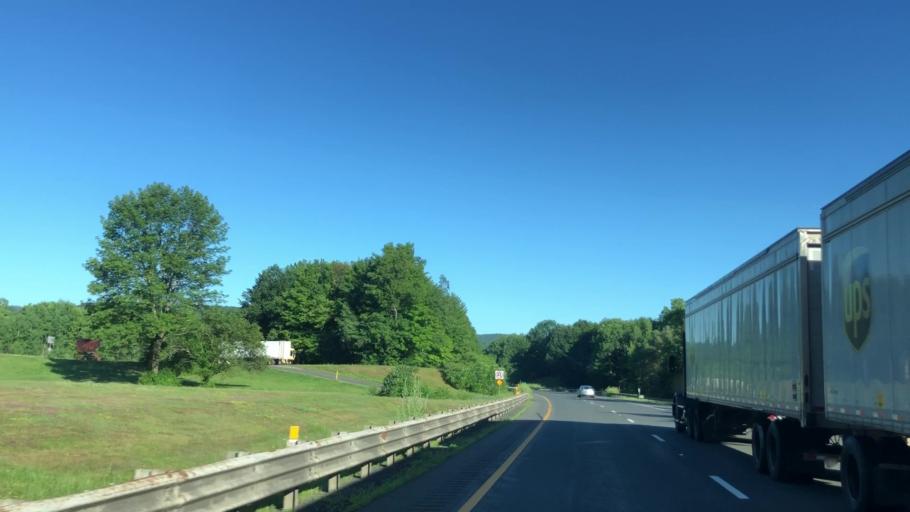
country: US
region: Massachusetts
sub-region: Berkshire County
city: West Stockbridge
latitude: 42.3415
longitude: -73.3920
